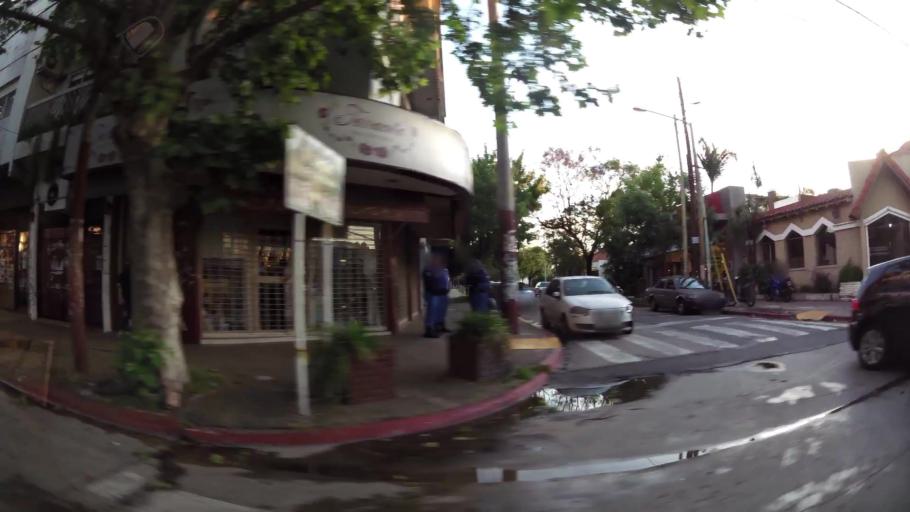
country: AR
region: Buenos Aires
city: Ituzaingo
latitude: -34.6504
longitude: -58.6468
